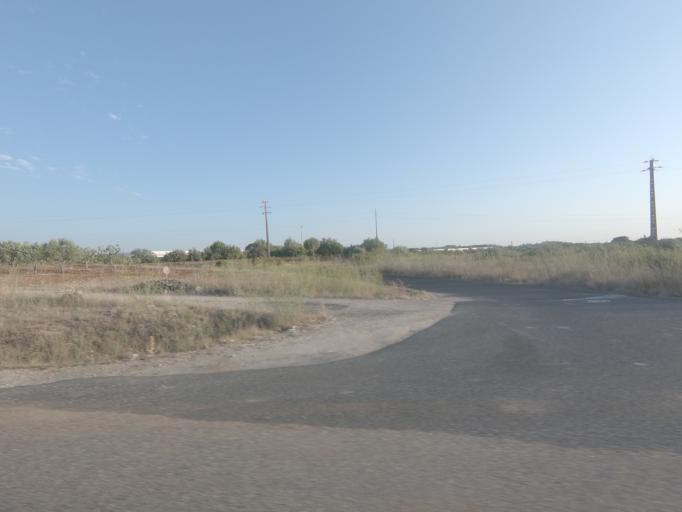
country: PT
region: Santarem
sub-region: Alcanena
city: Alcanena
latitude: 39.4822
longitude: -8.6278
